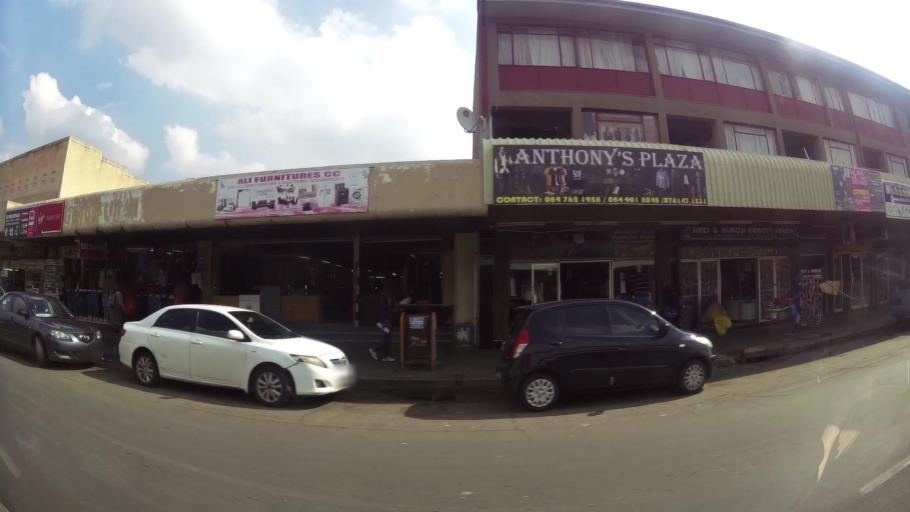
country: ZA
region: Gauteng
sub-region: Sedibeng District Municipality
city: Vereeniging
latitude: -26.6770
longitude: 27.9311
